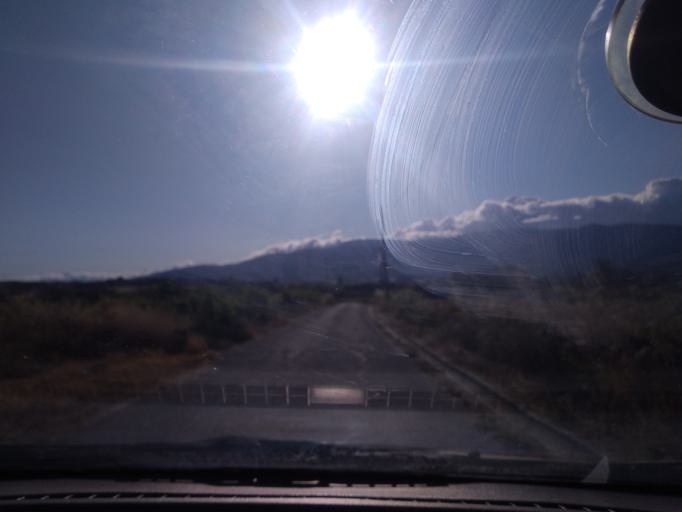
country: PT
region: Castelo Branco
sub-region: Covilha
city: Teixoso
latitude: 40.2585
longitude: -7.3999
